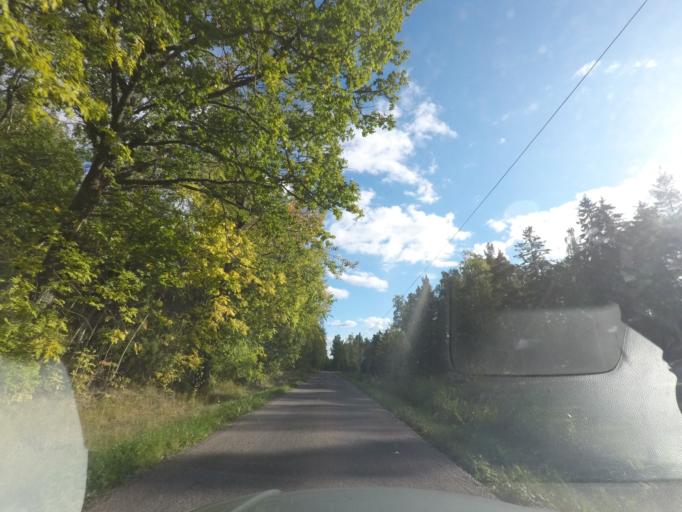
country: SE
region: Vaestmanland
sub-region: Hallstahammars Kommun
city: Kolback
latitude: 59.4957
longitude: 16.1894
